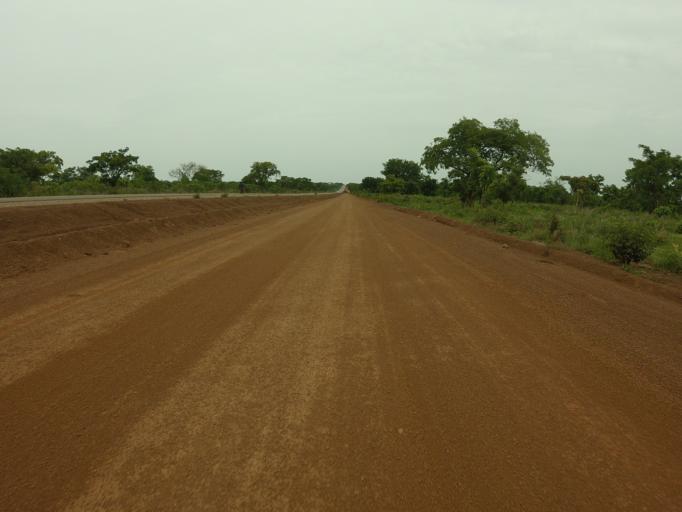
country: GH
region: Northern
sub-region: Yendi
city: Yendi
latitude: 9.0289
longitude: -0.0136
